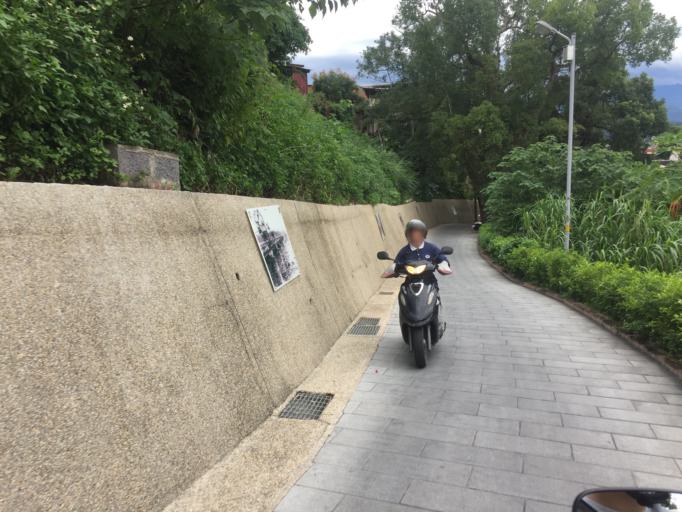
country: TW
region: Taiwan
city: Daxi
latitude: 24.7897
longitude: 121.1756
